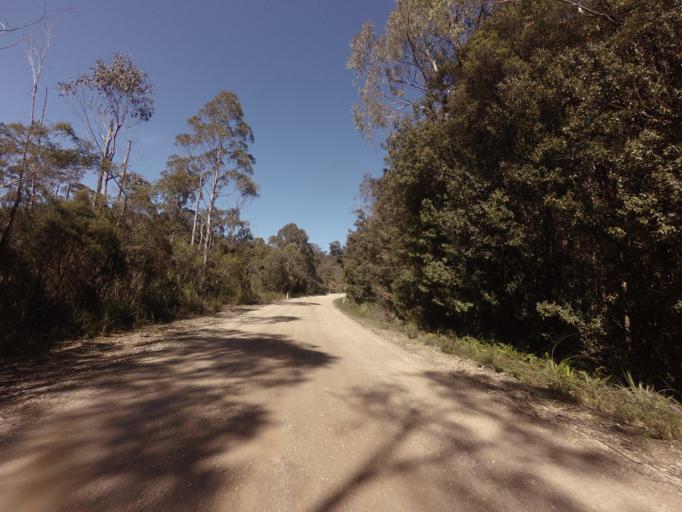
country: AU
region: Tasmania
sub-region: Huon Valley
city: Geeveston
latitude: -42.9051
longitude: 146.3695
